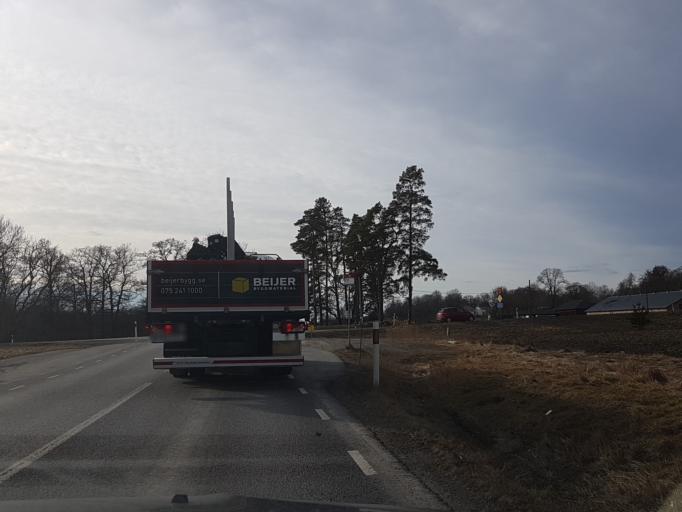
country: SE
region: Stockholm
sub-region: Norrtalje Kommun
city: Norrtalje
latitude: 59.6796
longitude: 18.6846
